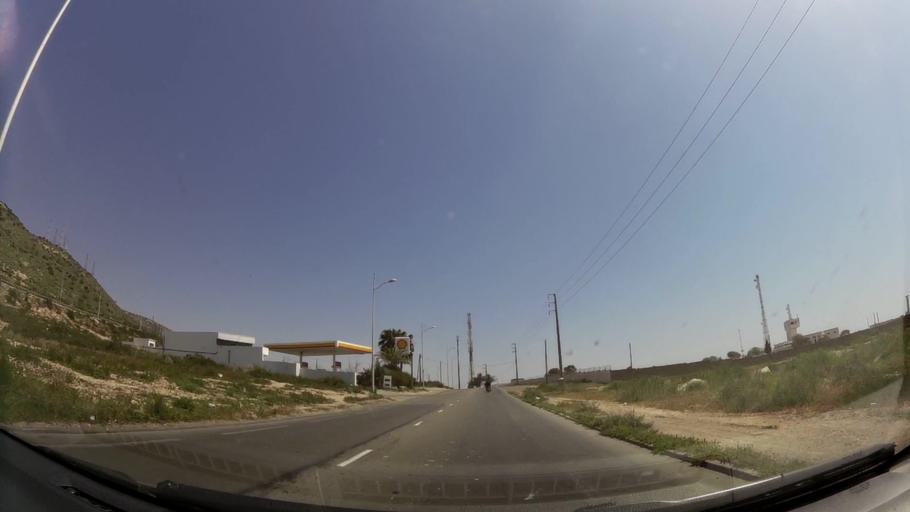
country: MA
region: Souss-Massa-Draa
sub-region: Agadir-Ida-ou-Tnan
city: Agadir
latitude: 30.4352
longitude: -9.6432
